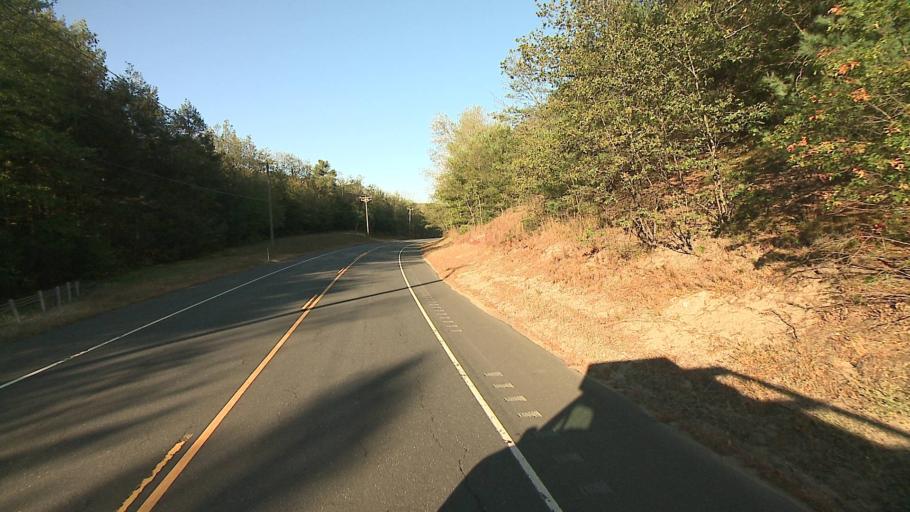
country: US
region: Connecticut
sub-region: Hartford County
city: Collinsville
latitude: 41.8193
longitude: -72.9618
